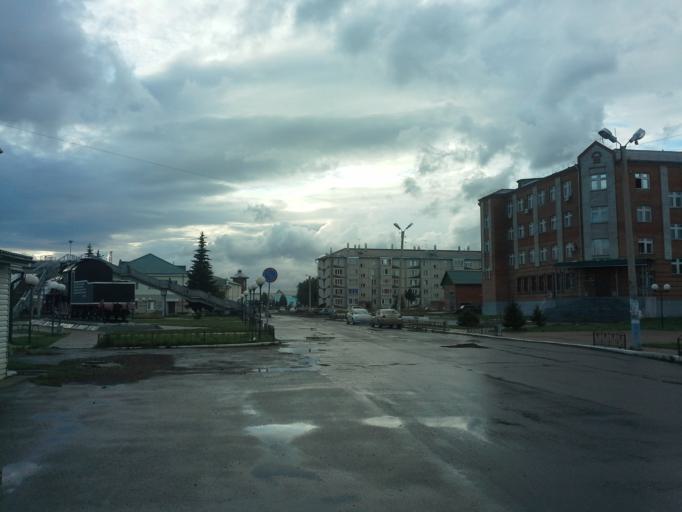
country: RU
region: Krasnoyarskiy
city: Ilanskiy
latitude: 56.2398
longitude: 96.0710
